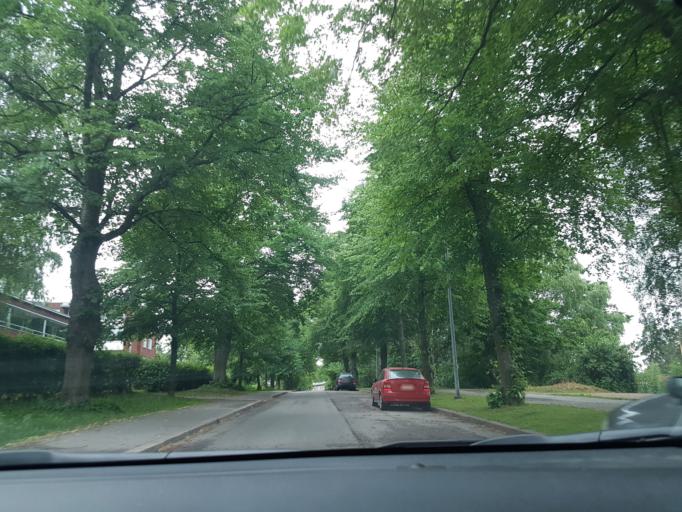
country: FI
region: Uusimaa
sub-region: Helsinki
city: Vantaa
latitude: 60.2157
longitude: 25.0980
